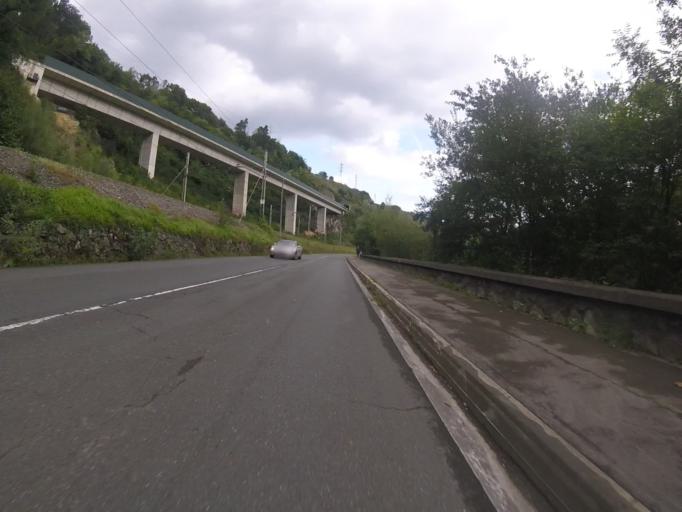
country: ES
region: Basque Country
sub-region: Provincia de Guipuzcoa
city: Tolosa
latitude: 43.1283
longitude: -2.0877
